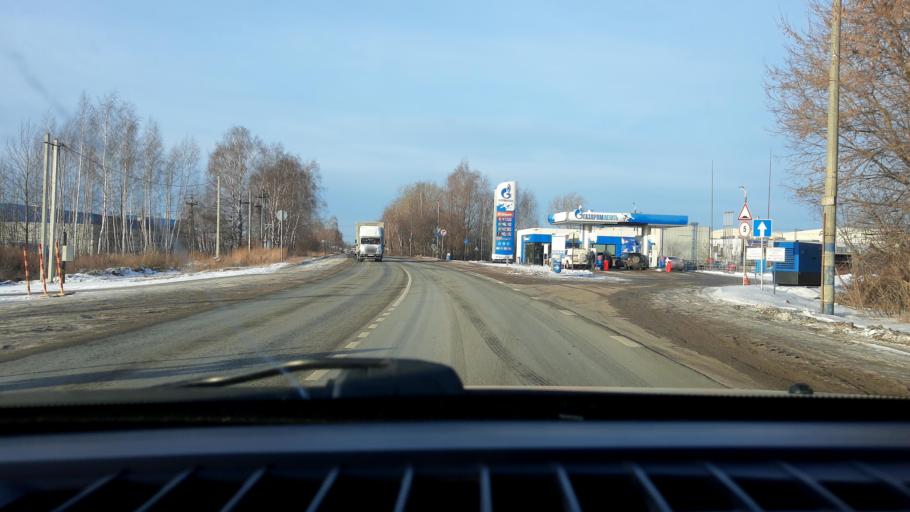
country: RU
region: Nizjnij Novgorod
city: Bor
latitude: 56.3769
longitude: 44.0574
